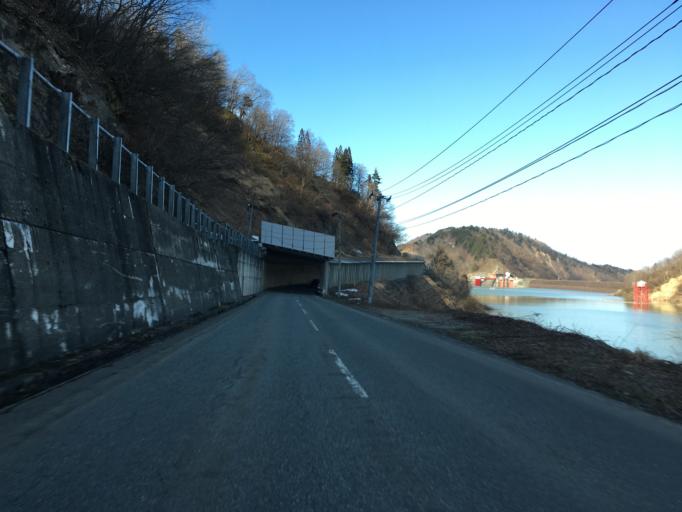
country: JP
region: Yamagata
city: Nagai
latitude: 37.9668
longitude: 139.9133
